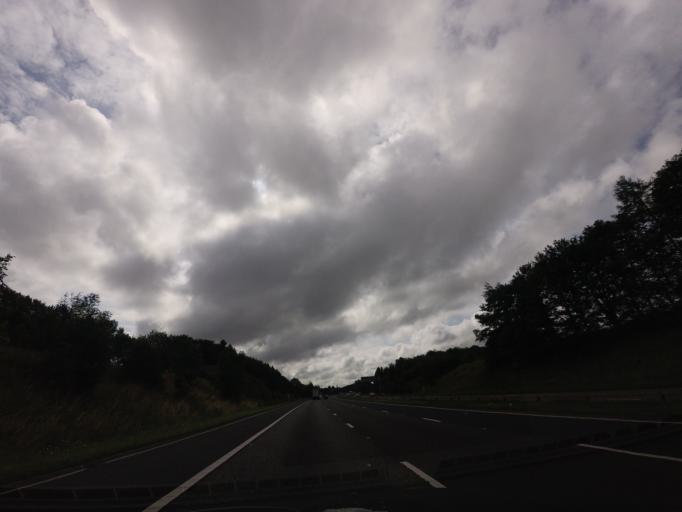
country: GB
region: England
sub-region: Cumbria
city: Penrith
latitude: 54.6444
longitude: -2.7396
